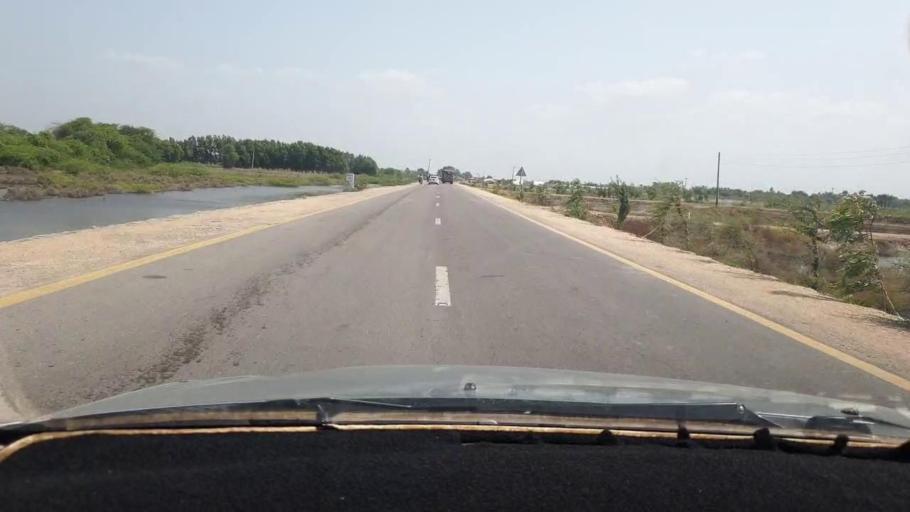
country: PK
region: Sindh
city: Digri
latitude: 25.1572
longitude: 69.1213
